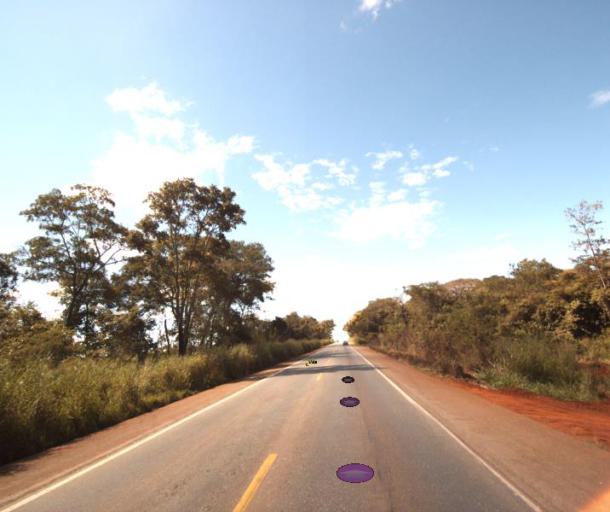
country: BR
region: Goias
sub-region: Rialma
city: Rialma
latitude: -15.4062
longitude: -49.5314
